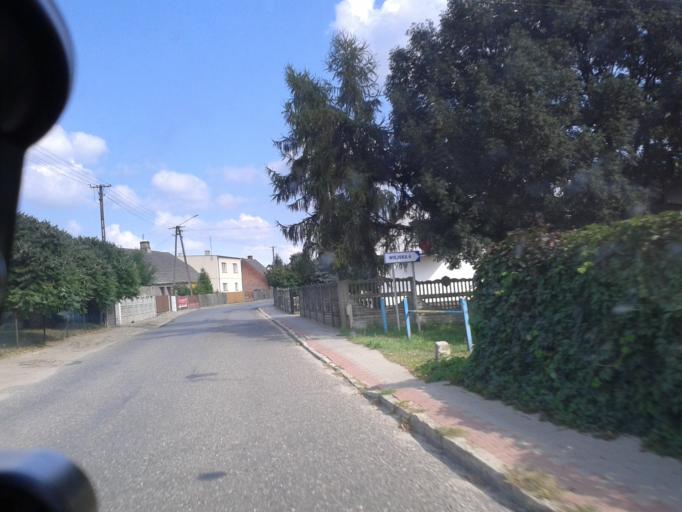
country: PL
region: Greater Poland Voivodeship
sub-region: Powiat szamotulski
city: Obrzycko
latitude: 52.7133
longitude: 16.5253
